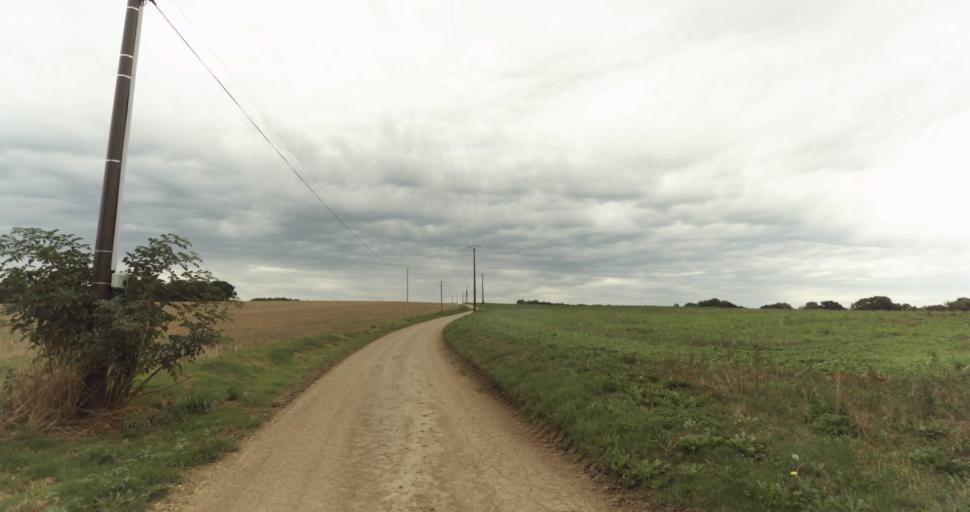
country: FR
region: Lower Normandy
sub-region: Departement de l'Orne
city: Gace
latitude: 48.6841
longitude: 0.2798
